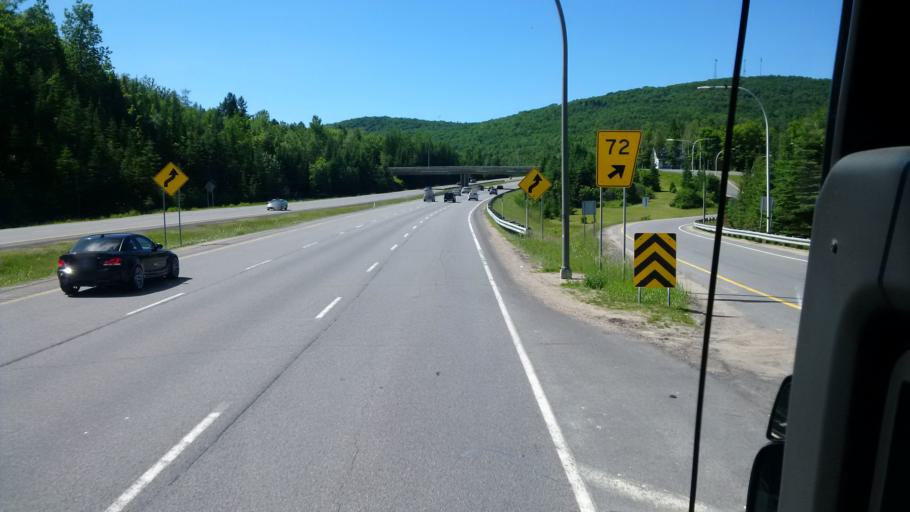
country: CA
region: Quebec
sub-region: Laurentides
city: Sainte-Adele
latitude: 45.9732
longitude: -74.1561
